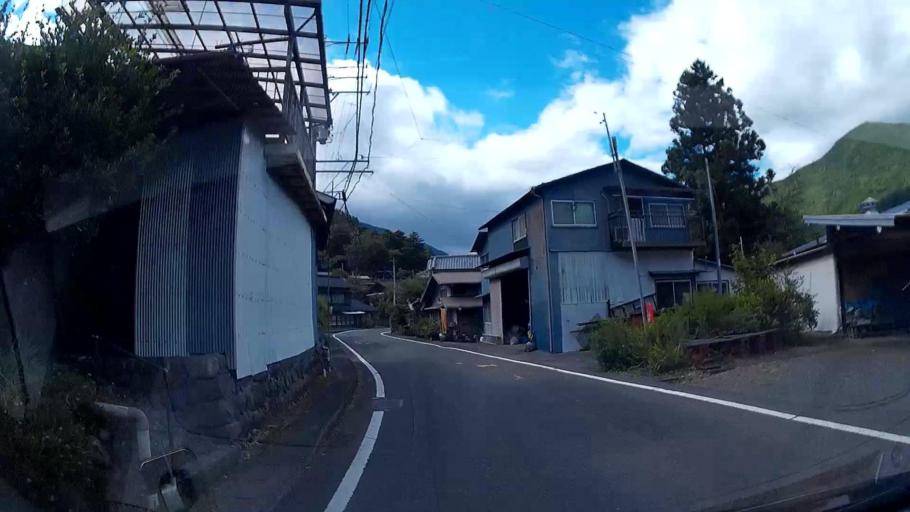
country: JP
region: Shizuoka
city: Shizuoka-shi
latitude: 35.2490
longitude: 138.2424
